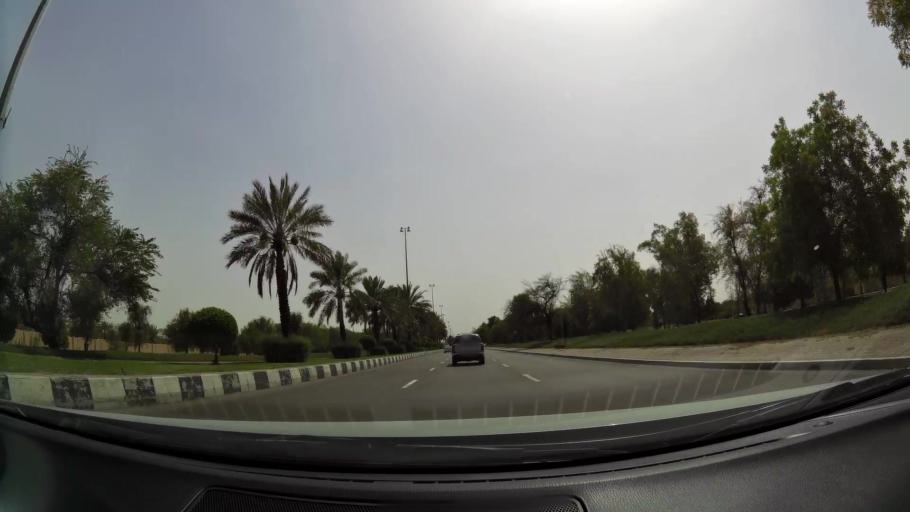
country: AE
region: Abu Dhabi
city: Al Ain
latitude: 24.1879
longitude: 55.6391
